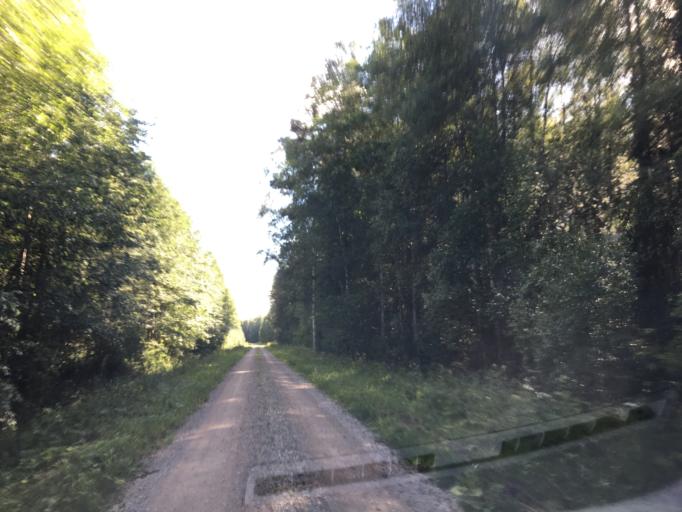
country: EE
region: Viljandimaa
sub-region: Suure-Jaani vald
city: Suure-Jaani
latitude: 58.5237
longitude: 25.2866
